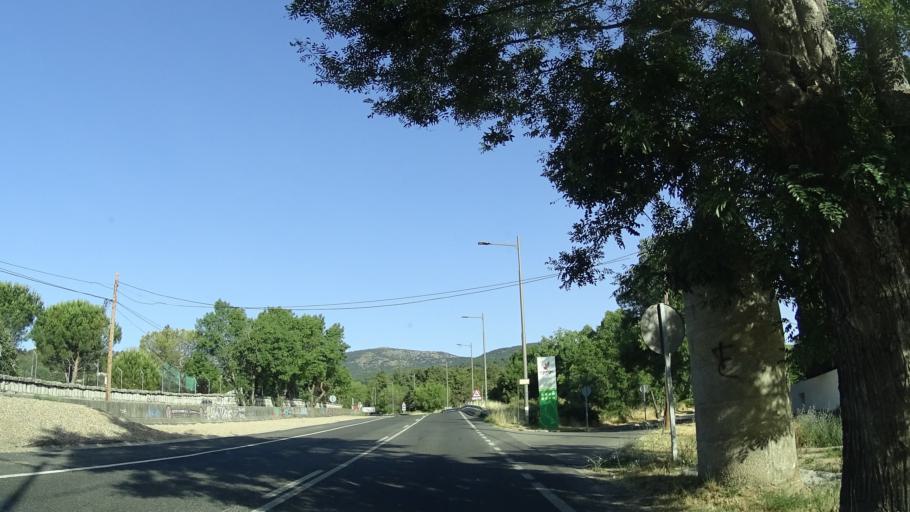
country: ES
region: Madrid
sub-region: Provincia de Madrid
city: Guadarrama
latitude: 40.6774
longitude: -4.1010
